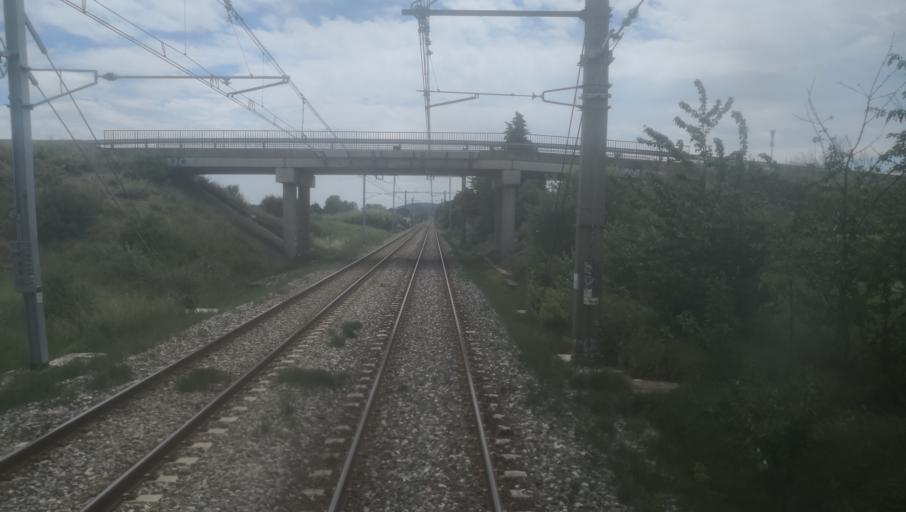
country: FR
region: Languedoc-Roussillon
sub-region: Departement de l'Herault
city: Mireval
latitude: 43.5085
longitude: 3.8099
